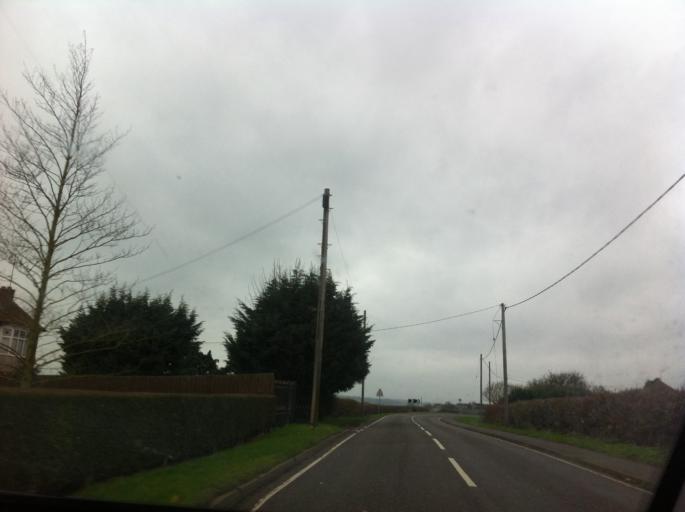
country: GB
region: England
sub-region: Northamptonshire
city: Bozeat
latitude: 52.2596
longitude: -0.6865
